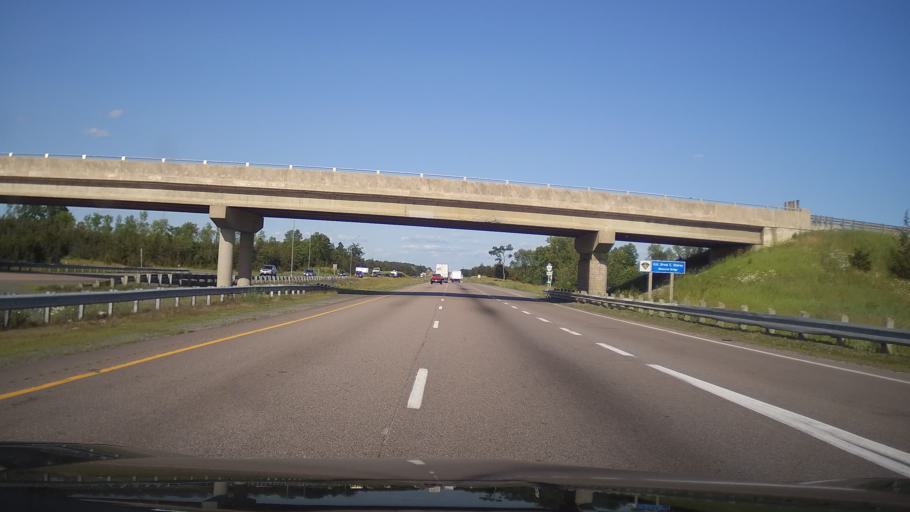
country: CA
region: Ontario
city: Deseronto
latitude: 44.2443
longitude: -77.0641
